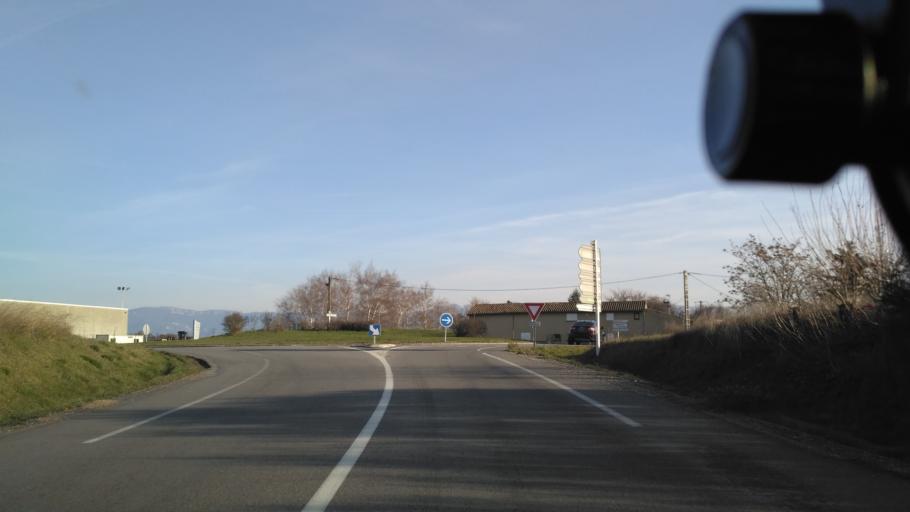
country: FR
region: Rhone-Alpes
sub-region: Departement de la Drome
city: Alixan
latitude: 44.9972
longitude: 4.9995
